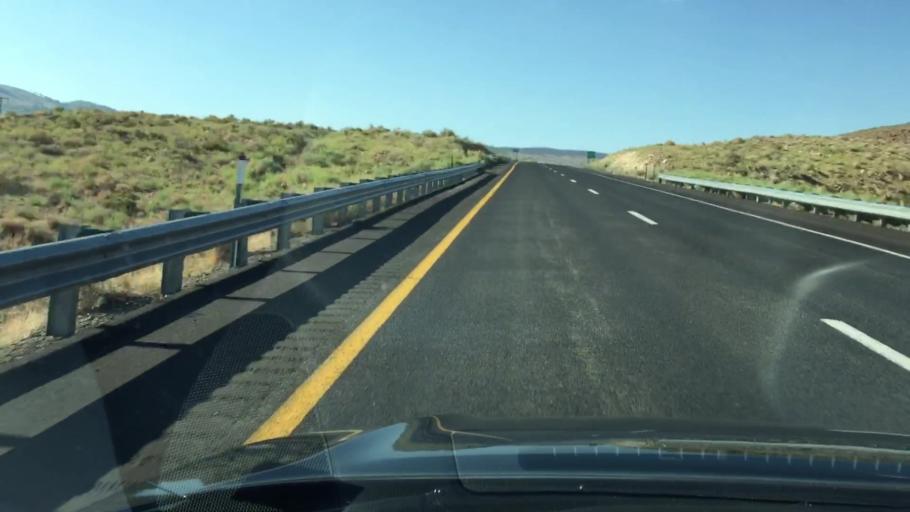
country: US
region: California
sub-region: Inyo County
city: West Bishop
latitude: 37.4616
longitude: -118.5774
